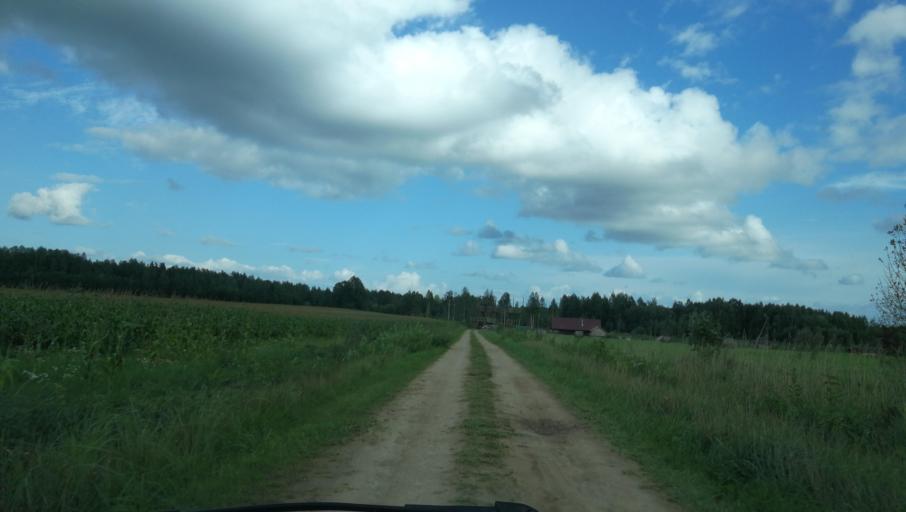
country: LV
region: Malpils
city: Malpils
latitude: 56.9173
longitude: 25.0053
